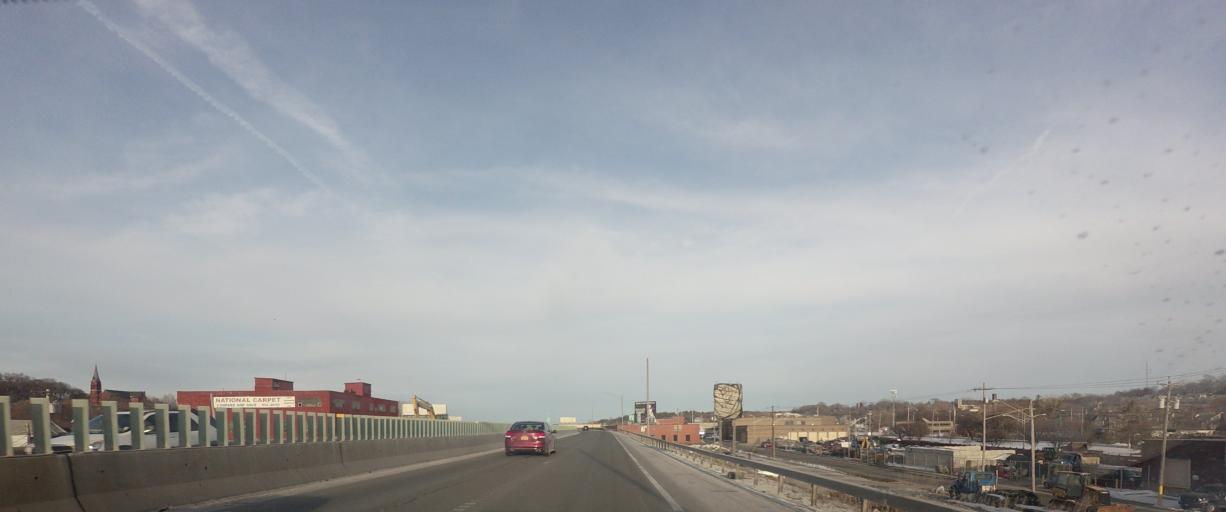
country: US
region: New York
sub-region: Onondaga County
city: Syracuse
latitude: 43.0513
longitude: -76.1304
